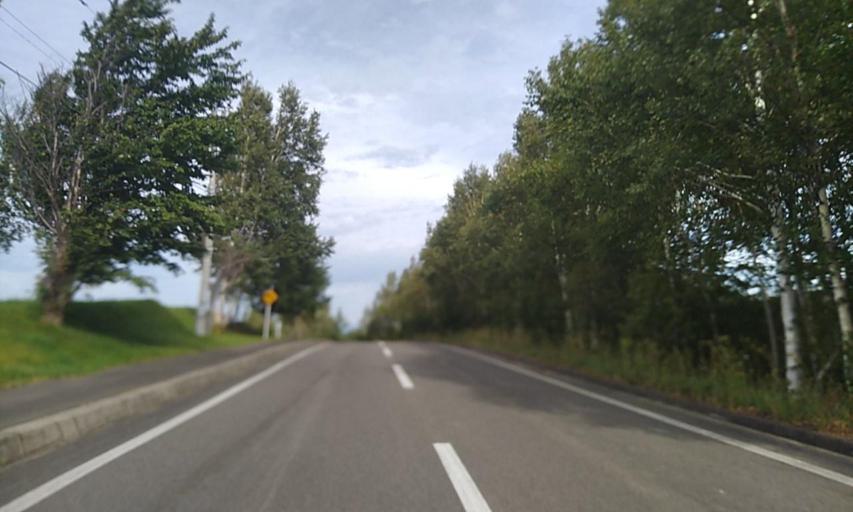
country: JP
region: Hokkaido
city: Abashiri
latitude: 43.7969
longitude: 144.5730
